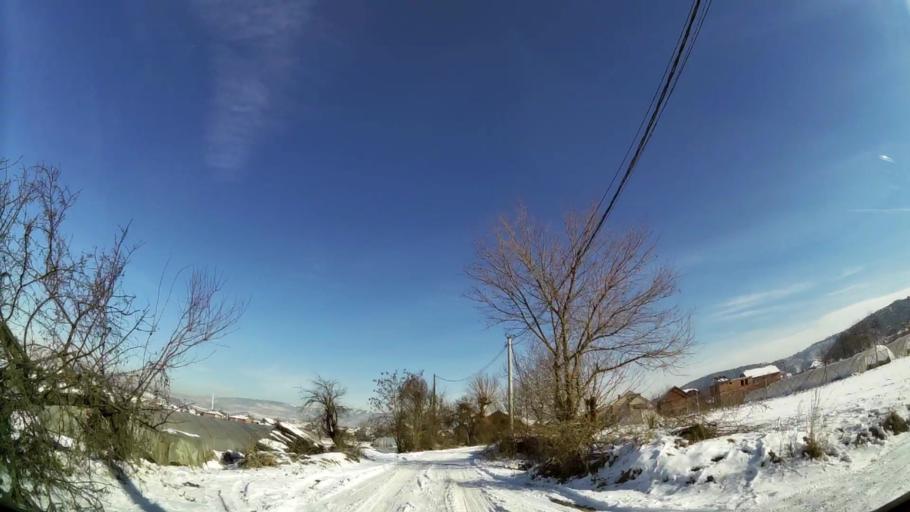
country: MK
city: Grchec
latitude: 41.9858
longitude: 21.3279
